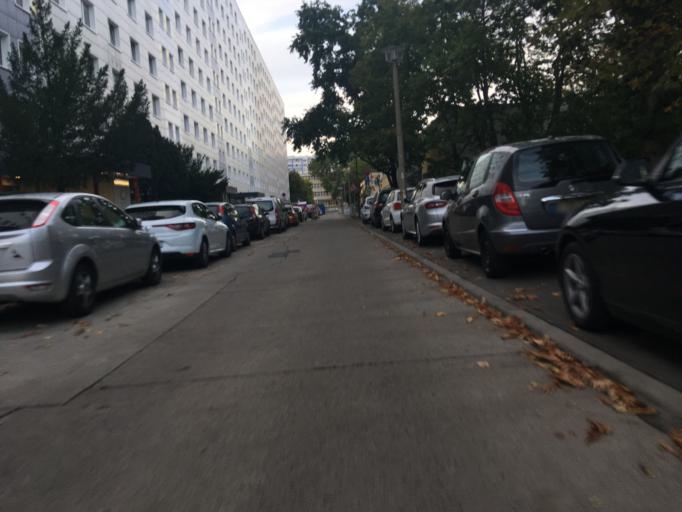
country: DE
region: Berlin
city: Fennpfuhl
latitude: 52.5297
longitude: 13.4809
